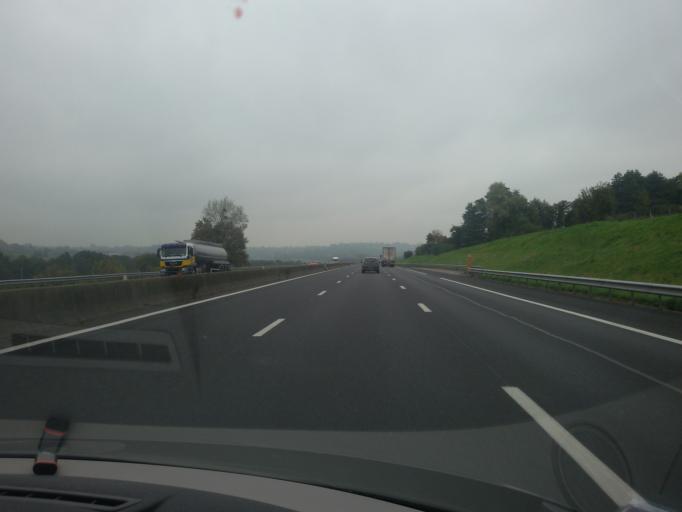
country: FR
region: Lower Normandy
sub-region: Departement du Calvados
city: Saint-Gatien-des-Bois
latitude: 49.2996
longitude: 0.2566
